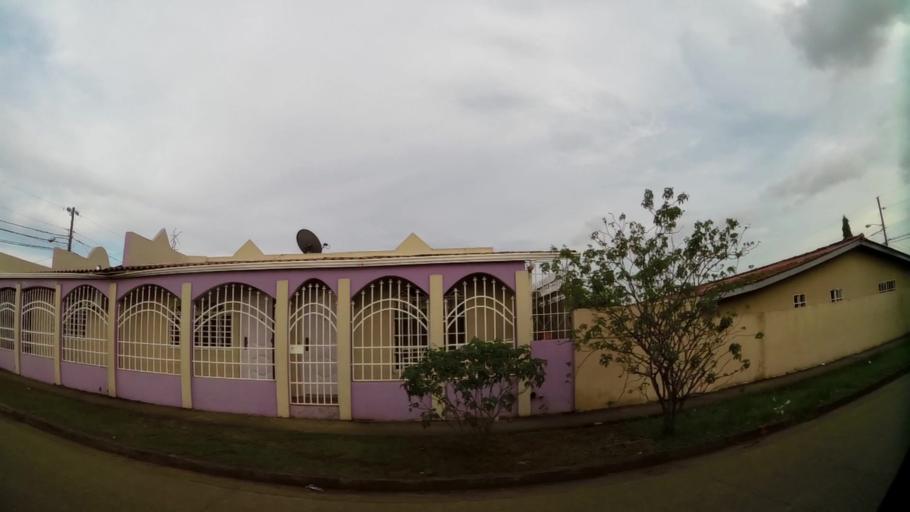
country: PA
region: Panama
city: Tocumen
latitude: 9.0959
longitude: -79.3874
